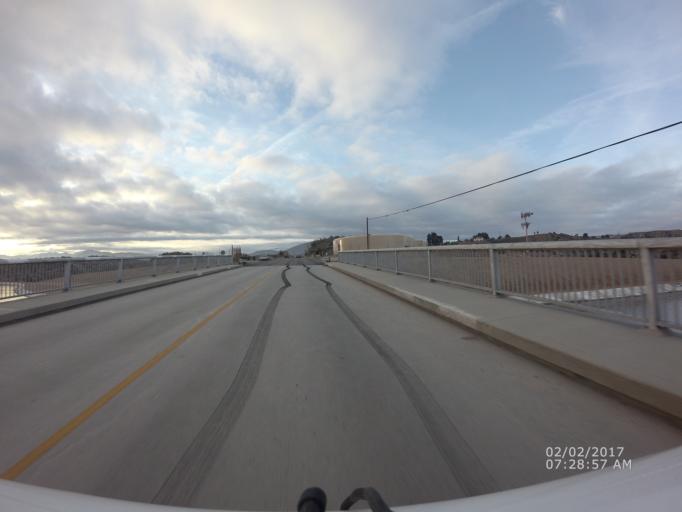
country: US
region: California
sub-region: Los Angeles County
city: Littlerock
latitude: 34.5304
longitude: -118.0453
